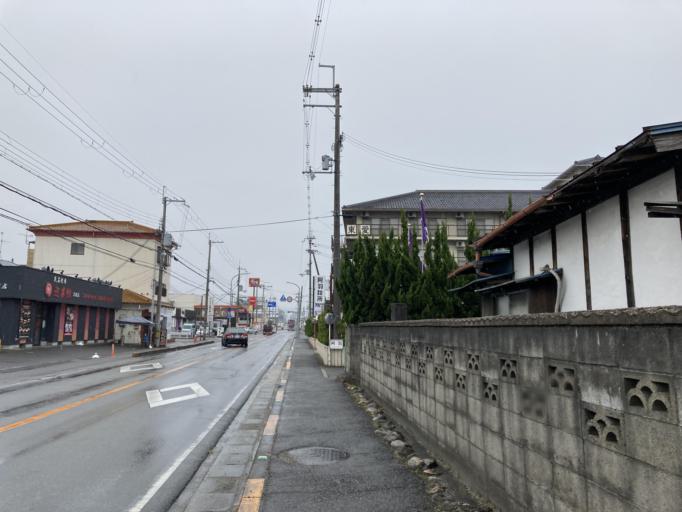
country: JP
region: Nara
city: Tenri
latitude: 34.5907
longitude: 135.8364
